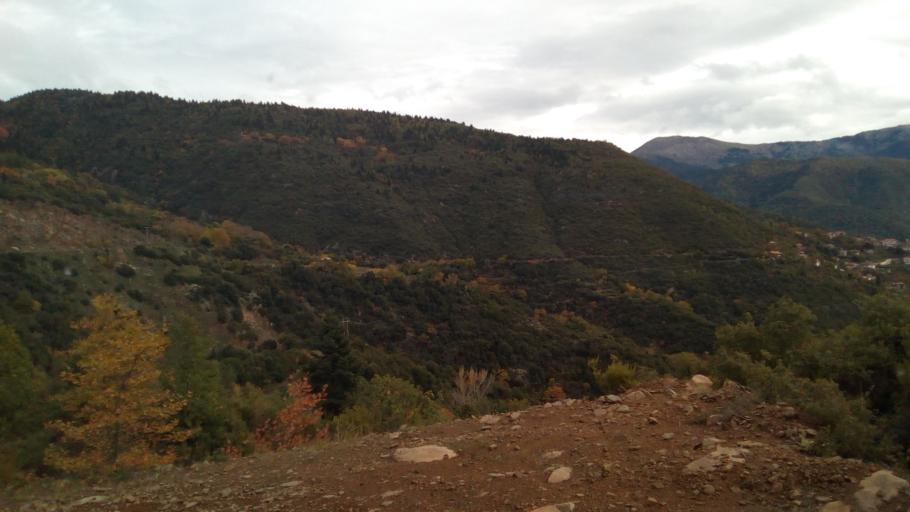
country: GR
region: West Greece
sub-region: Nomos Aitolias kai Akarnanias
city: Nafpaktos
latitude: 38.5605
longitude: 21.9576
